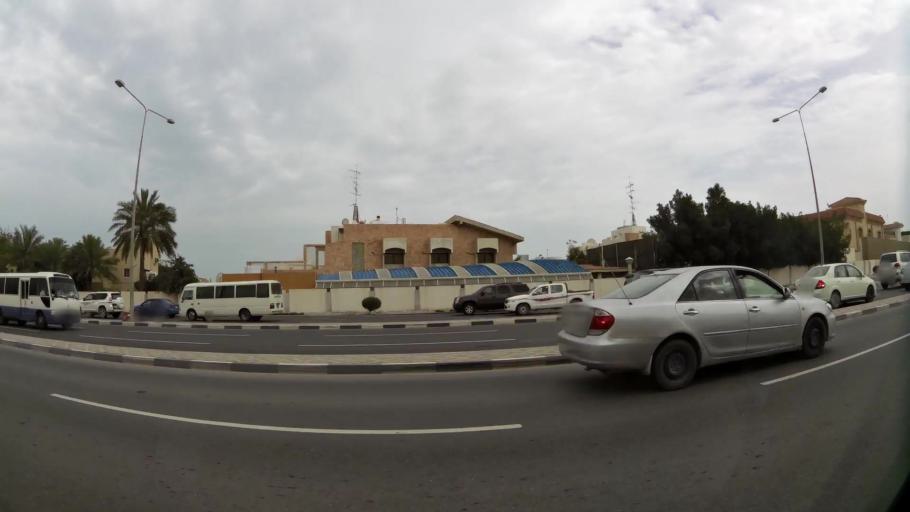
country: QA
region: Baladiyat ad Dawhah
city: Doha
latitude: 25.3301
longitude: 51.5056
